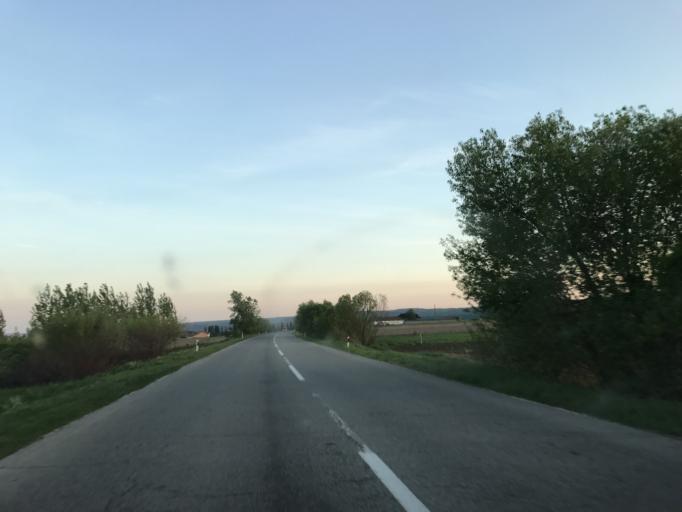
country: RS
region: Central Serbia
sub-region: Borski Okrug
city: Negotin
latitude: 44.2564
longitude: 22.5192
